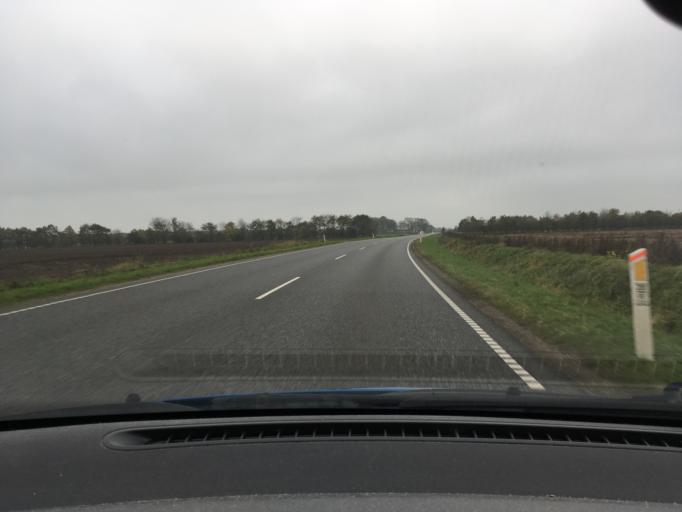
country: DK
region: South Denmark
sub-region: Tonder Kommune
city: Toftlund
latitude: 55.0636
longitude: 9.1472
